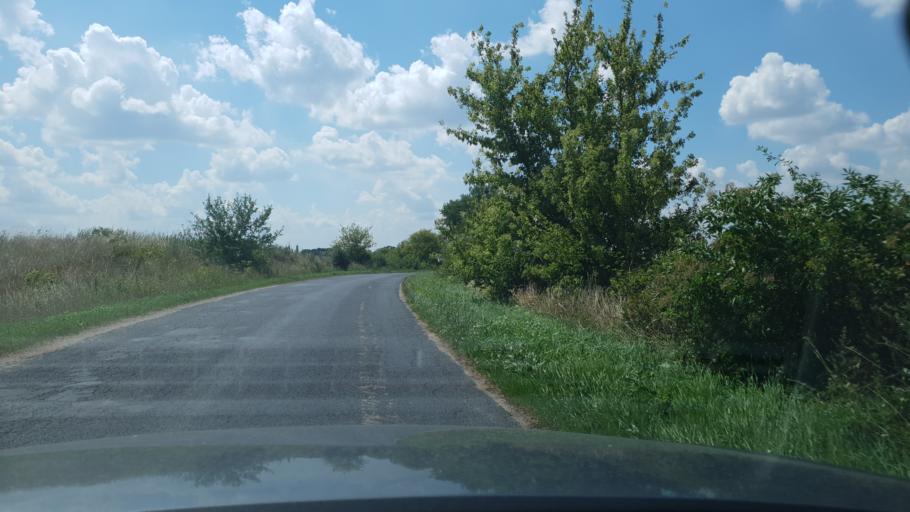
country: PL
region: Kujawsko-Pomorskie
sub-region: Powiat wabrzeski
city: Pluznica
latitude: 53.3006
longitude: 18.8062
